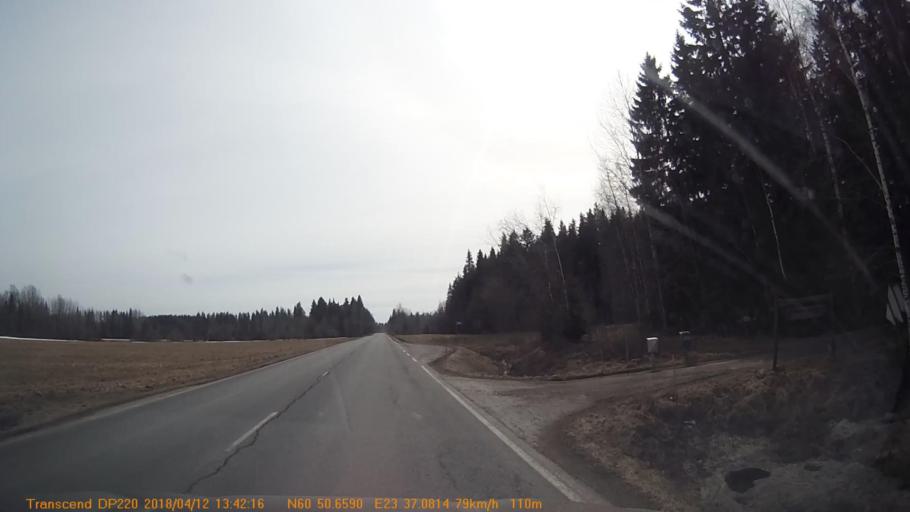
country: FI
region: Haeme
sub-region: Forssa
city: Forssa
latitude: 60.8436
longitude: 23.6180
